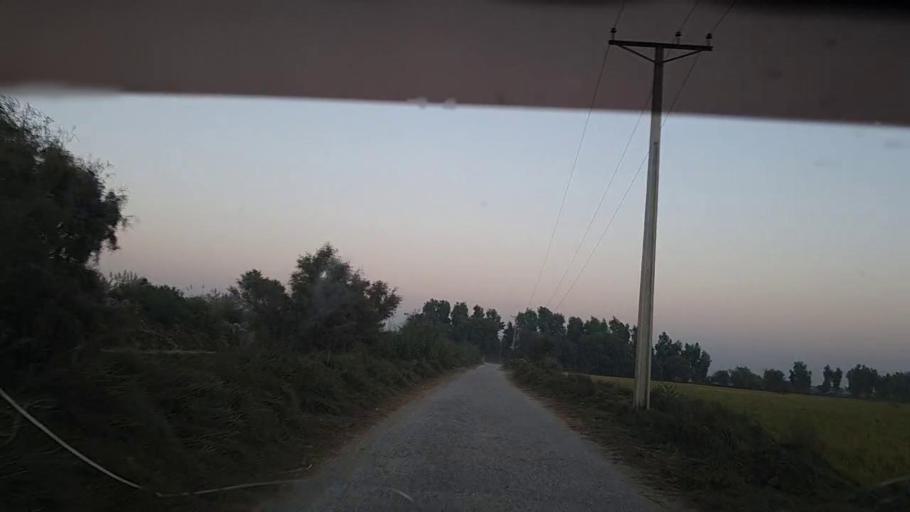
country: PK
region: Sindh
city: Ratodero
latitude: 27.8640
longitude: 68.2663
